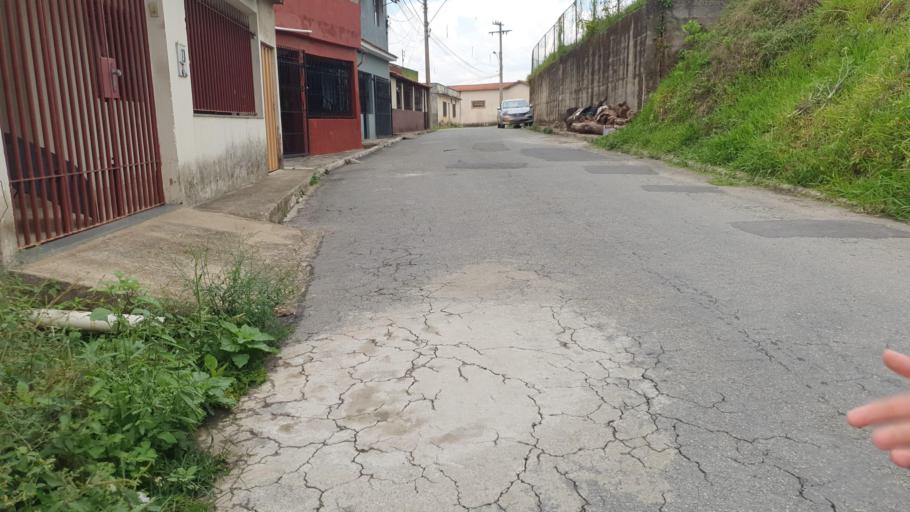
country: BR
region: Minas Gerais
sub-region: Sao Joao Del Rei
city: Sao Joao del Rei
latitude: -21.1265
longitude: -44.2646
